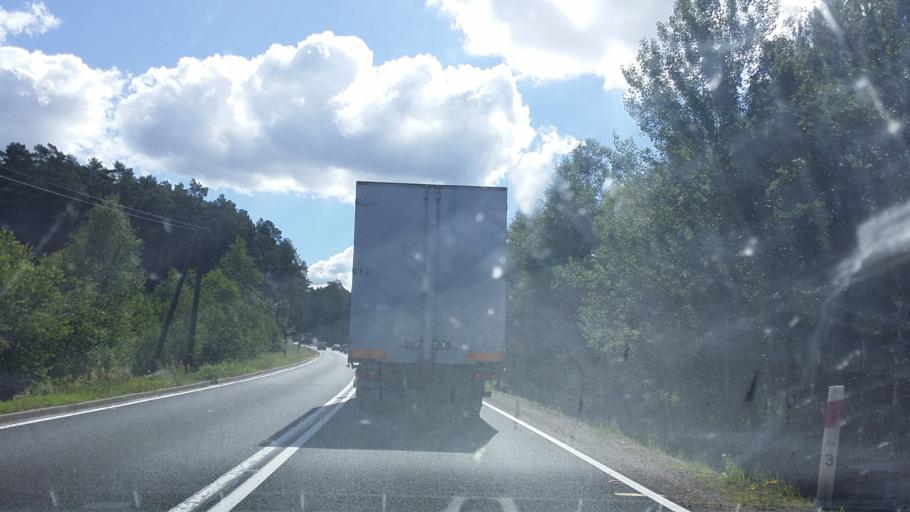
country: PL
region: West Pomeranian Voivodeship
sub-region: Powiat choszczenski
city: Drawno
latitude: 53.3028
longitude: 15.7902
